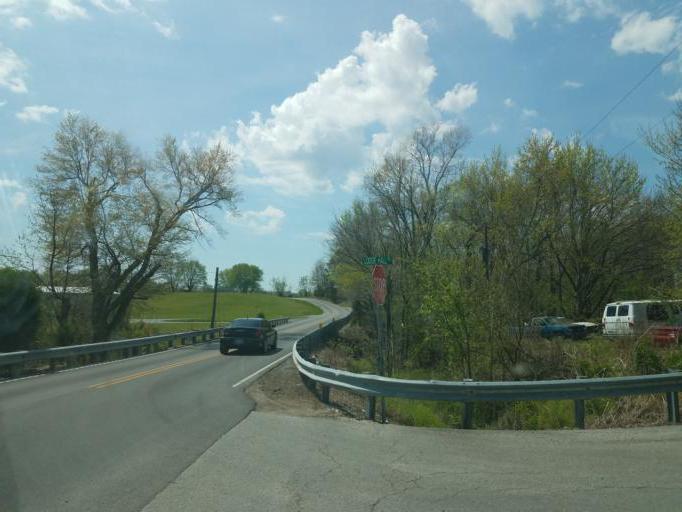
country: US
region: Kentucky
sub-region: Warren County
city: Bowling Green
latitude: 37.1164
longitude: -86.4235
